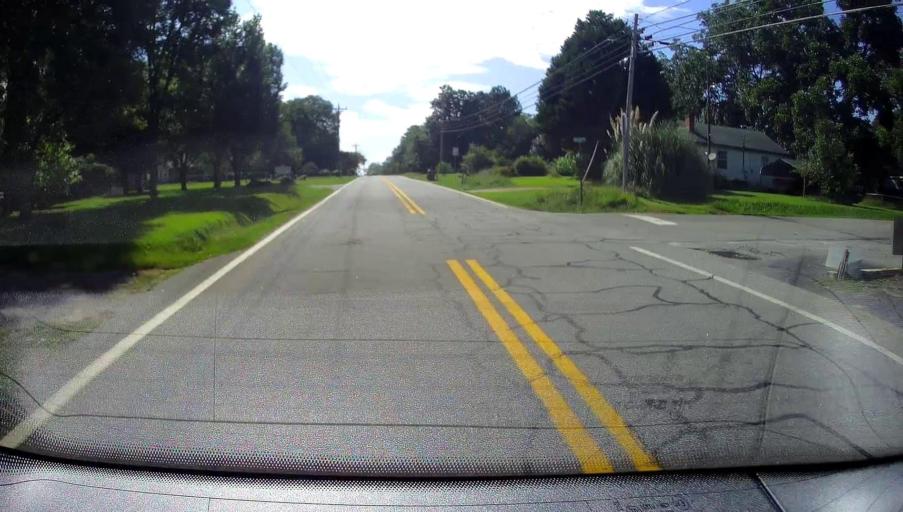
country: US
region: Georgia
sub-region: Upson County
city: Hannahs Mill
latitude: 32.9350
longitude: -84.3475
